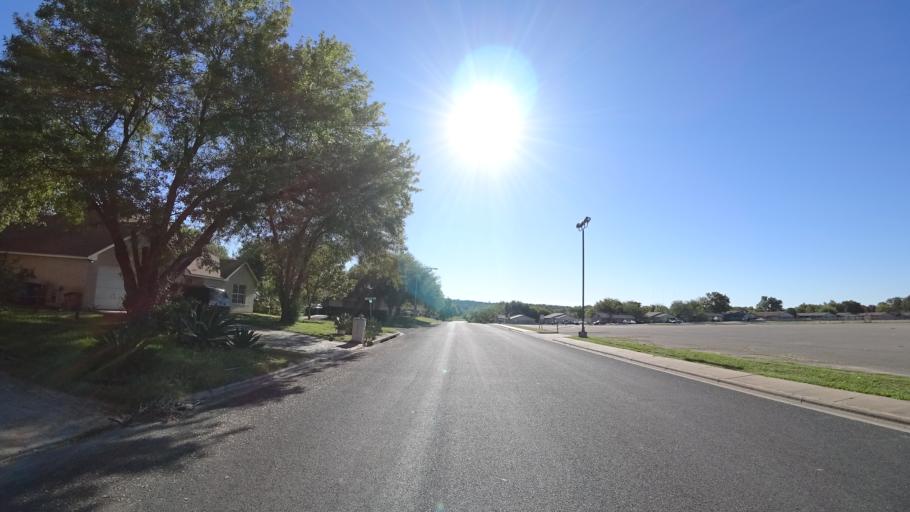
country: US
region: Texas
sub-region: Travis County
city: Hornsby Bend
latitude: 30.3137
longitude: -97.6540
